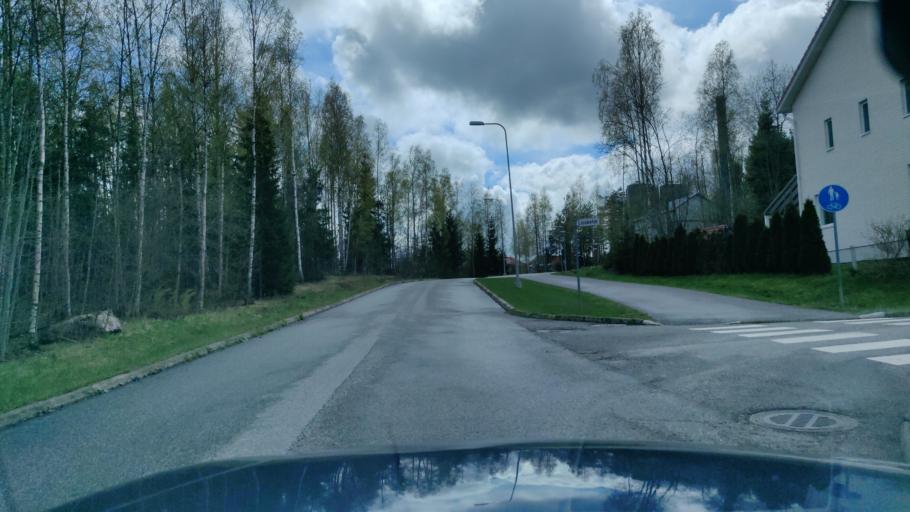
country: FI
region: Uusimaa
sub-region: Helsinki
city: Nurmijaervi
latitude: 60.3646
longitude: 24.7345
